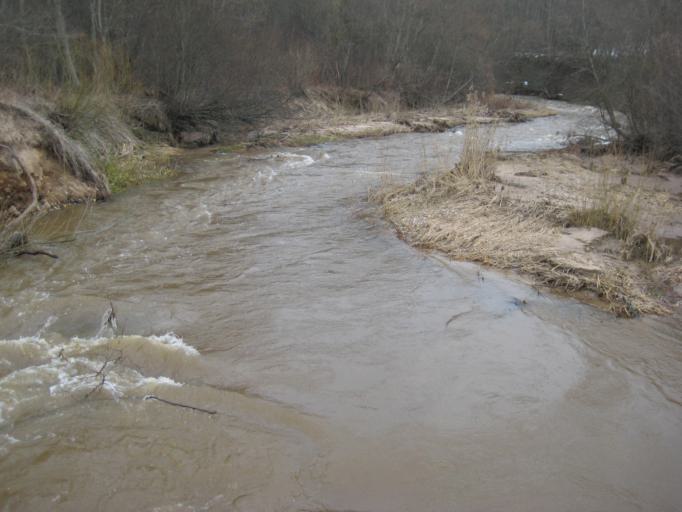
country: LT
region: Vilnius County
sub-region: Vilniaus Rajonas
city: Vievis
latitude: 54.8261
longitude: 24.9445
